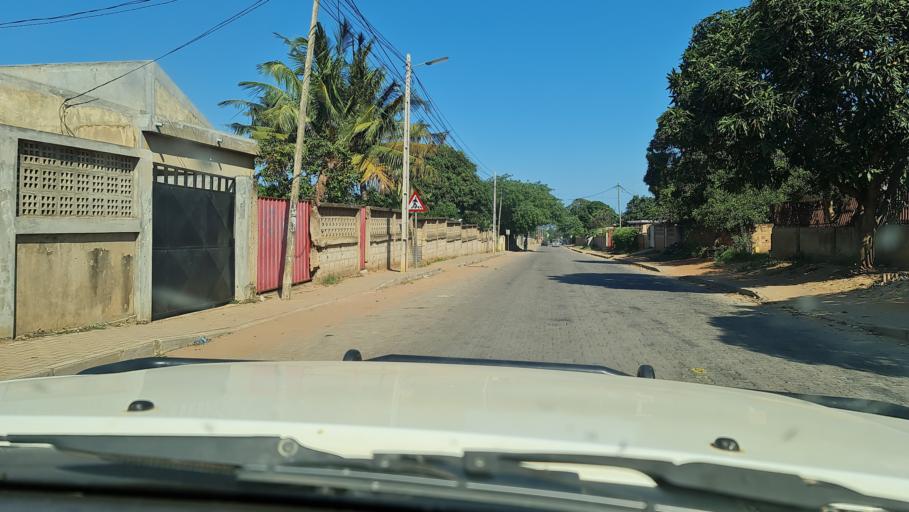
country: MZ
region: Maputo City
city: Maputo
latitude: -25.8411
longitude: 32.6390
